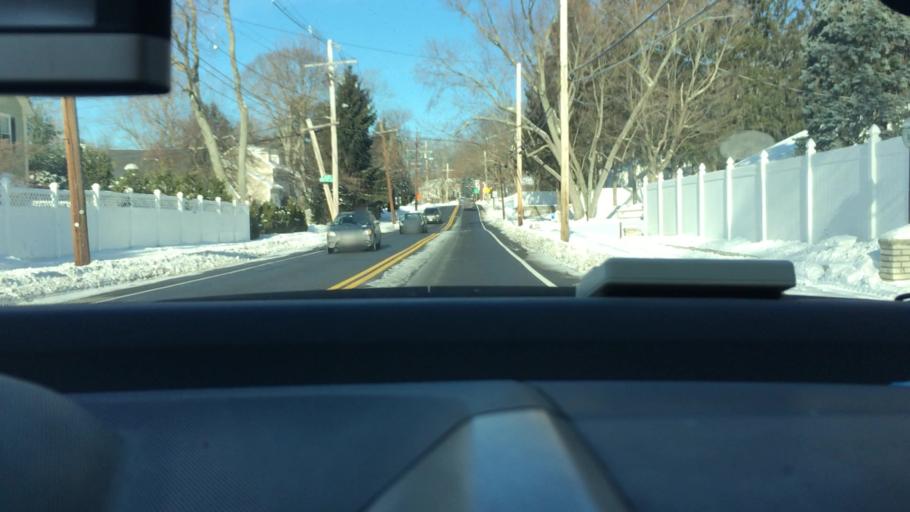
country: US
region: Massachusetts
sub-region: Middlesex County
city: Lexington
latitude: 42.4422
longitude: -71.1939
